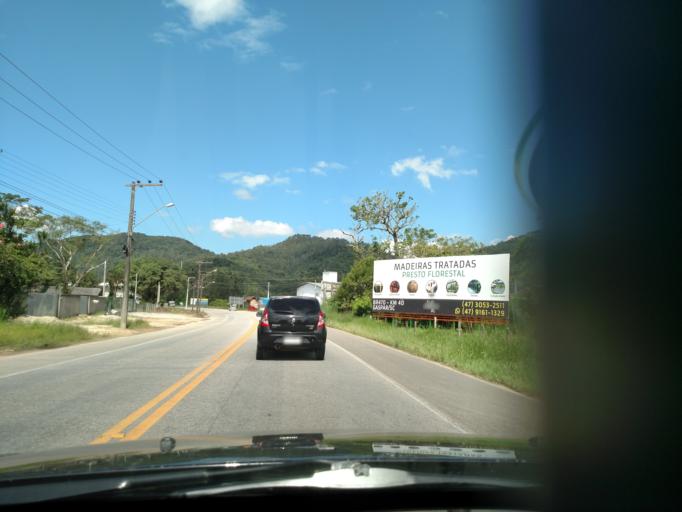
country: BR
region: Santa Catarina
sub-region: Itajai
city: Itajai
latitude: -26.8916
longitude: -48.7725
